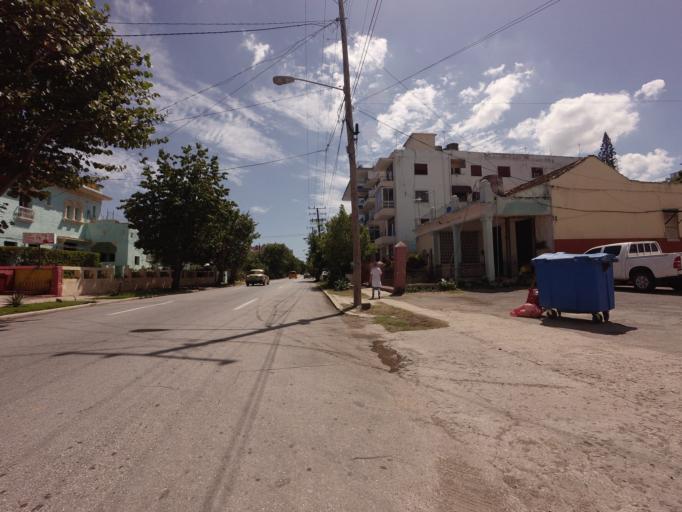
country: CU
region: La Habana
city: Havana
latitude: 23.1342
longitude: -82.4053
